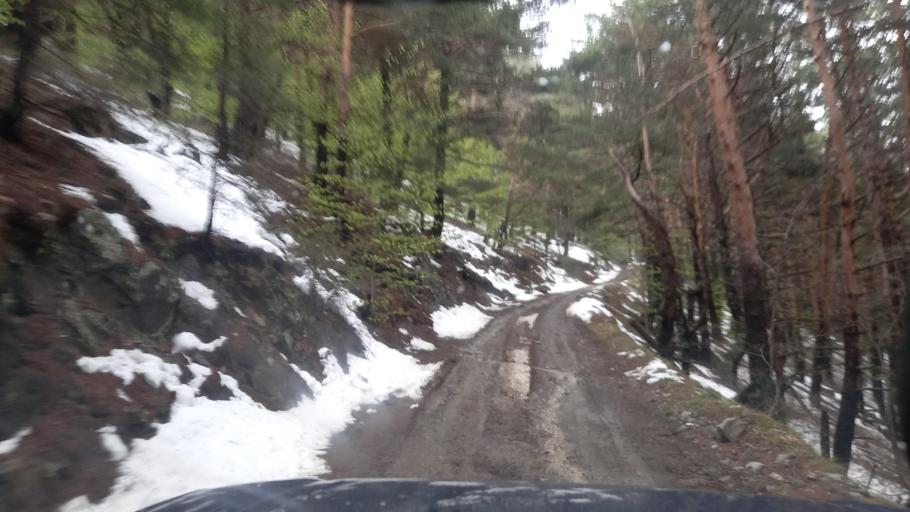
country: RU
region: North Ossetia
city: Mizur
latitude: 42.8035
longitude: 43.9619
